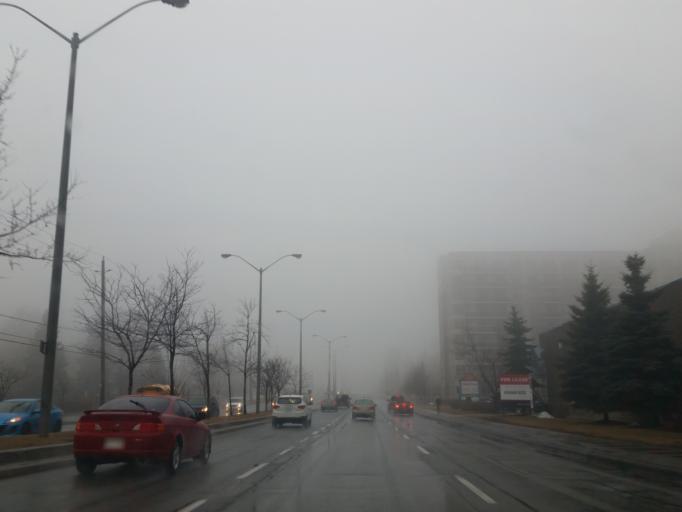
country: CA
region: Ontario
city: Scarborough
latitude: 43.7431
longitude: -79.2125
